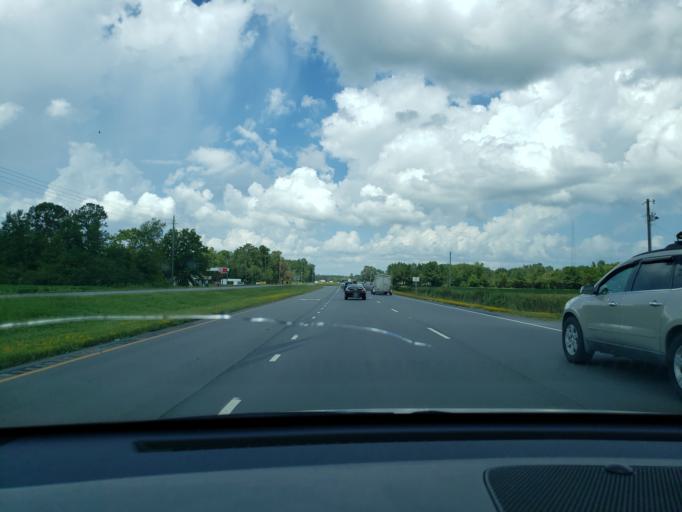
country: US
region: North Carolina
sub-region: Robeson County
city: Saint Pauls
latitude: 34.7836
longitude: -78.8114
